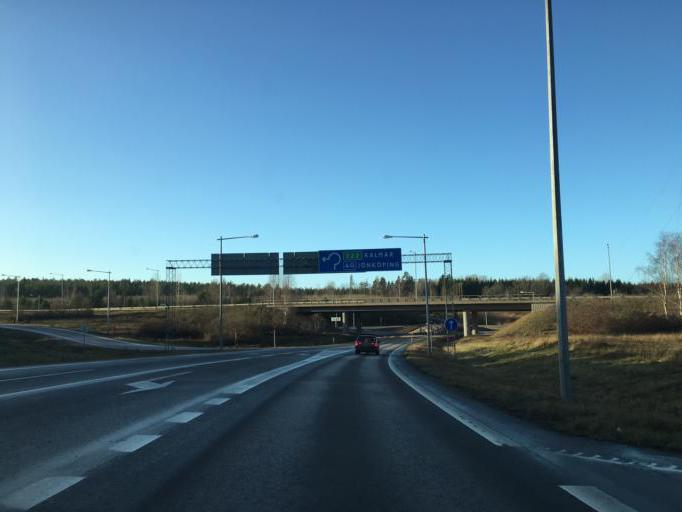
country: SE
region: Kalmar
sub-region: Vasterviks Kommun
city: Vaestervik
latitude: 57.7638
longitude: 16.5597
